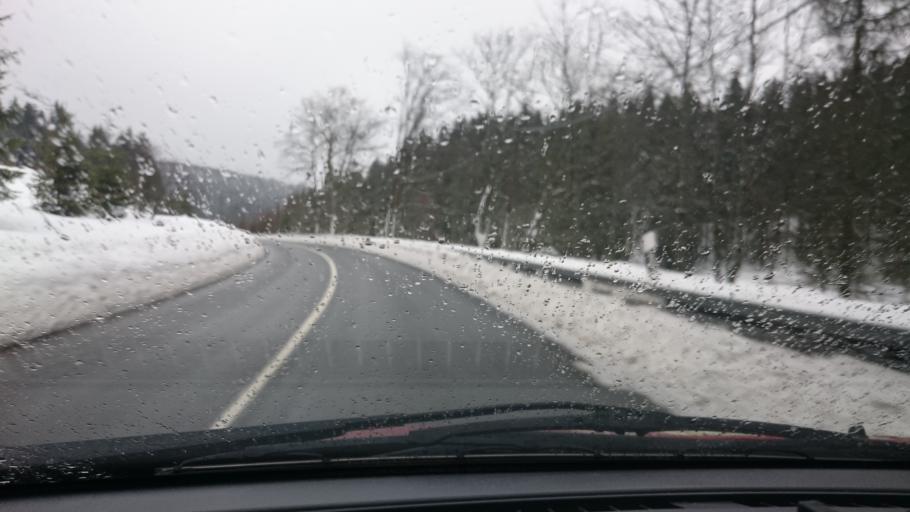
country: DE
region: Saxony
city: Tannenbergsthal
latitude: 50.4173
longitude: 12.4820
